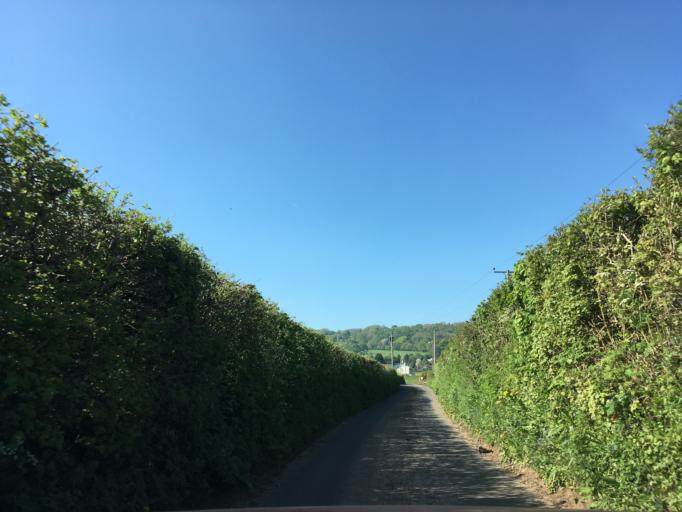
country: GB
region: Wales
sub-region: Newport
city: Llanvaches
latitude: 51.6211
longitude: -2.7964
